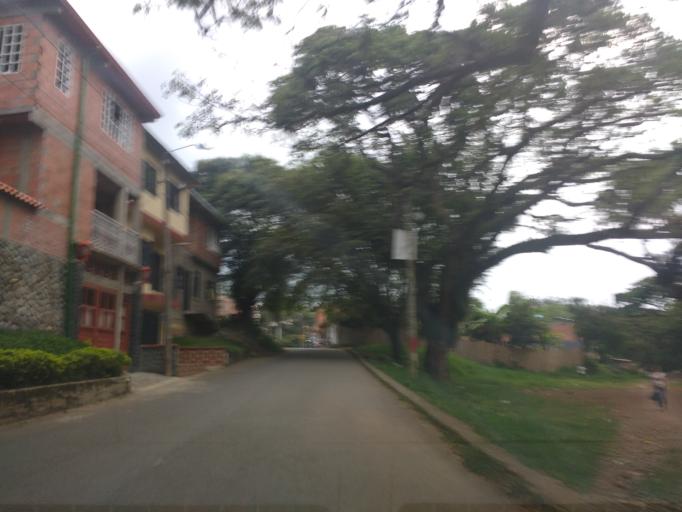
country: CO
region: Cauca
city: Santander de Quilichao
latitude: 3.0014
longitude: -76.4777
